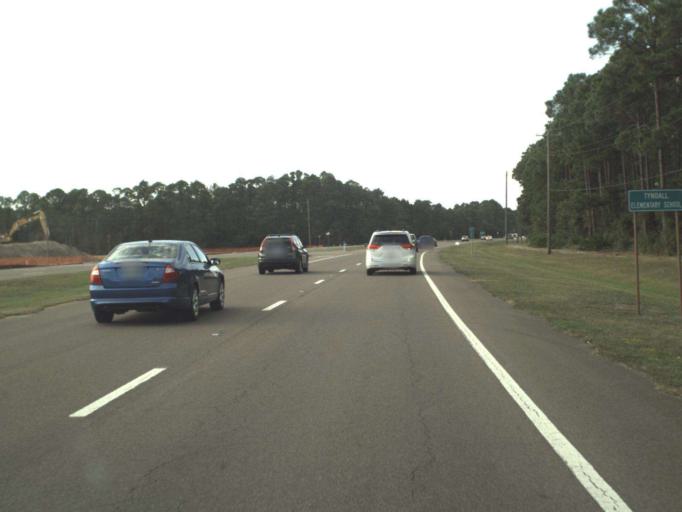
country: US
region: Florida
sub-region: Bay County
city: Tyndall Air Force Base
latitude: 30.0834
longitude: -85.6071
